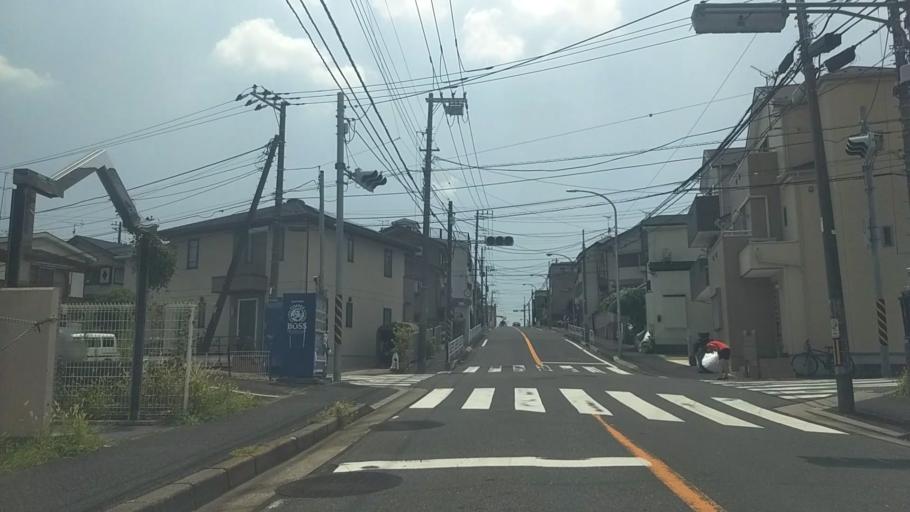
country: JP
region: Kanagawa
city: Yokohama
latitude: 35.5002
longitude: 139.6428
